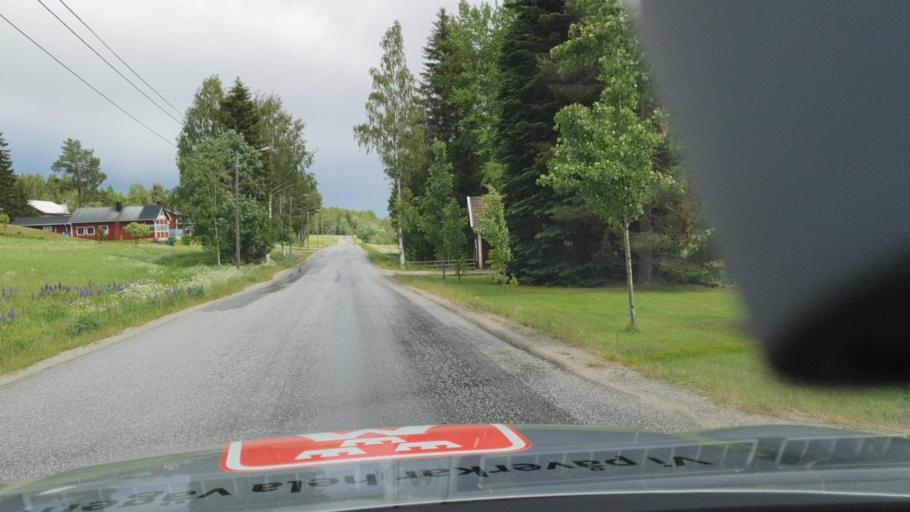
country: SE
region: Vaesternorrland
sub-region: OErnskoeldsviks Kommun
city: Bredbyn
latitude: 63.3319
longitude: 18.0679
